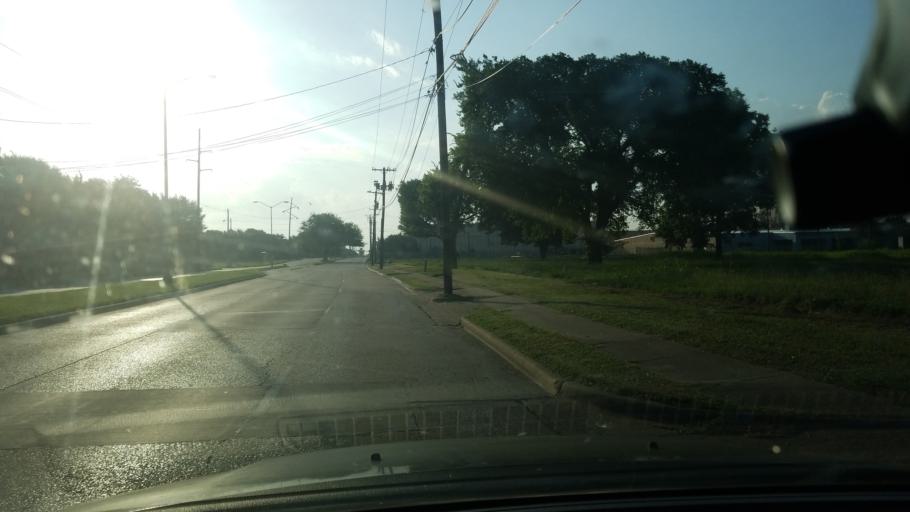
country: US
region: Texas
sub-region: Dallas County
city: Balch Springs
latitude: 32.7196
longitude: -96.6897
